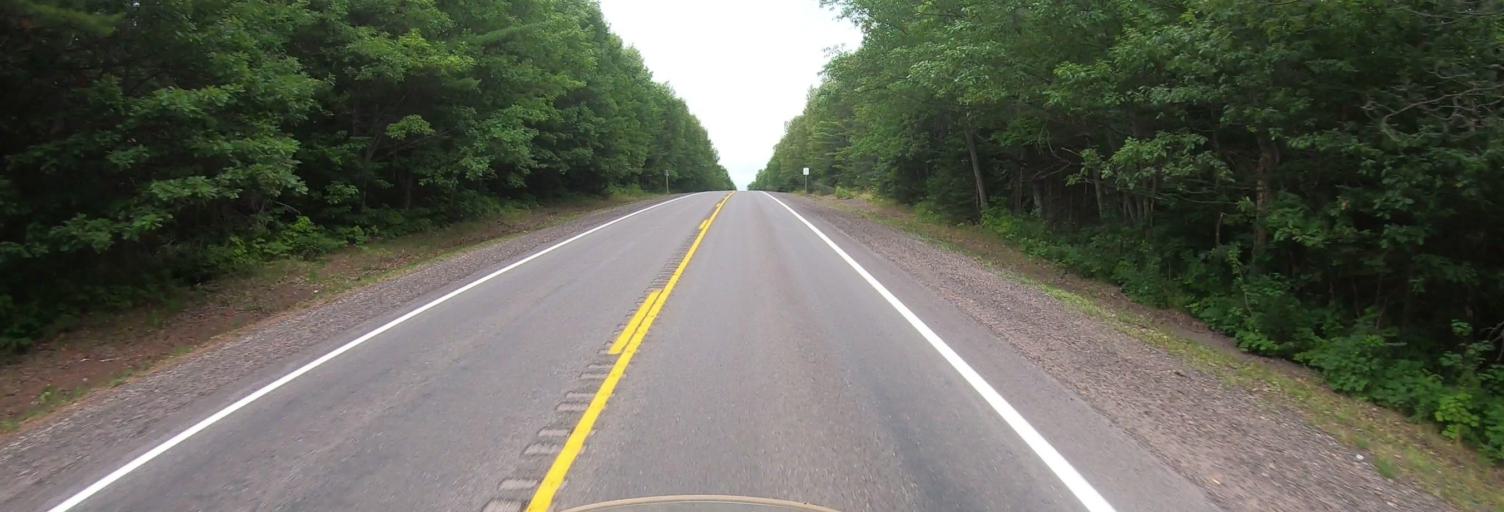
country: US
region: Michigan
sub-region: Keweenaw County
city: Eagle River
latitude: 47.3472
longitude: -88.3122
